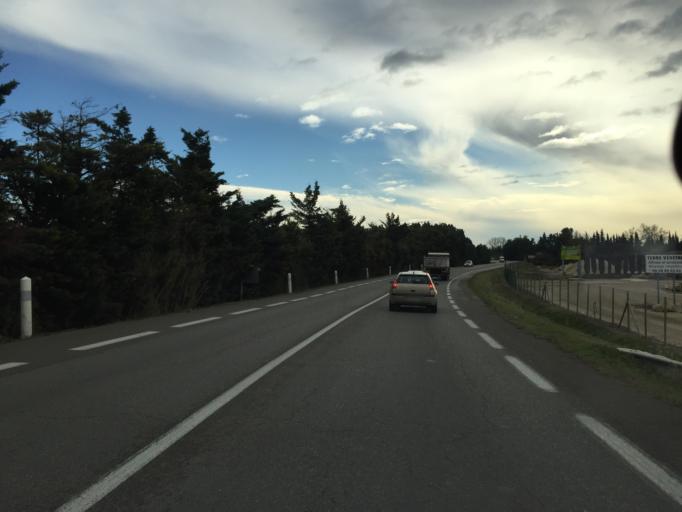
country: FR
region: Provence-Alpes-Cote d'Azur
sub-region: Departement du Vaucluse
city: L'Isle-sur-la-Sorgue
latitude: 43.9170
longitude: 5.0300
